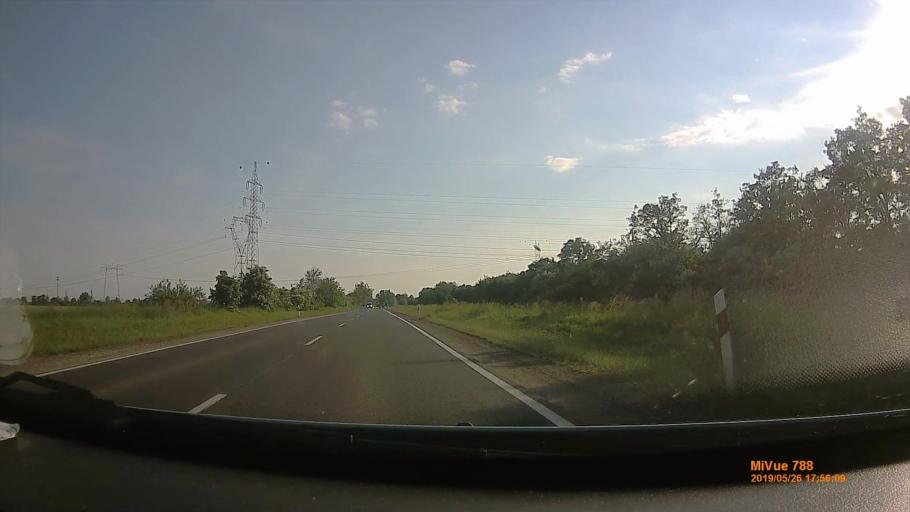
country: HU
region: Borsod-Abauj-Zemplen
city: Arnot
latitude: 48.1202
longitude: 20.8663
